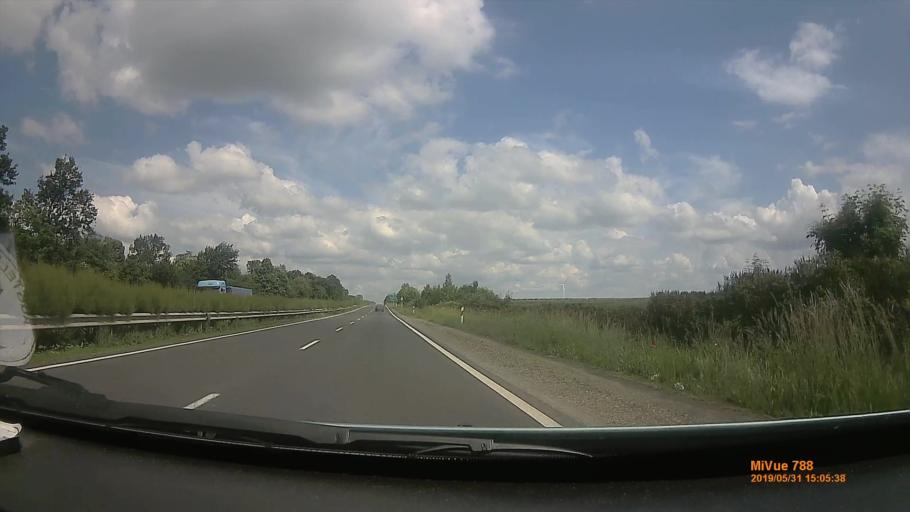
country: HU
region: Borsod-Abauj-Zemplen
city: Felsozsolca
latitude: 48.1112
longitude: 20.8771
